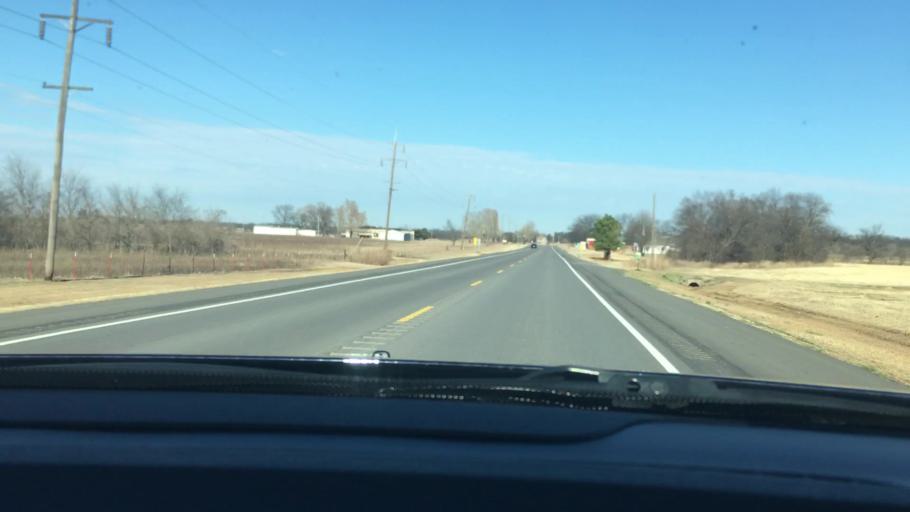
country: US
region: Oklahoma
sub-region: Garvin County
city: Wynnewood
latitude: 34.5890
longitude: -97.1425
